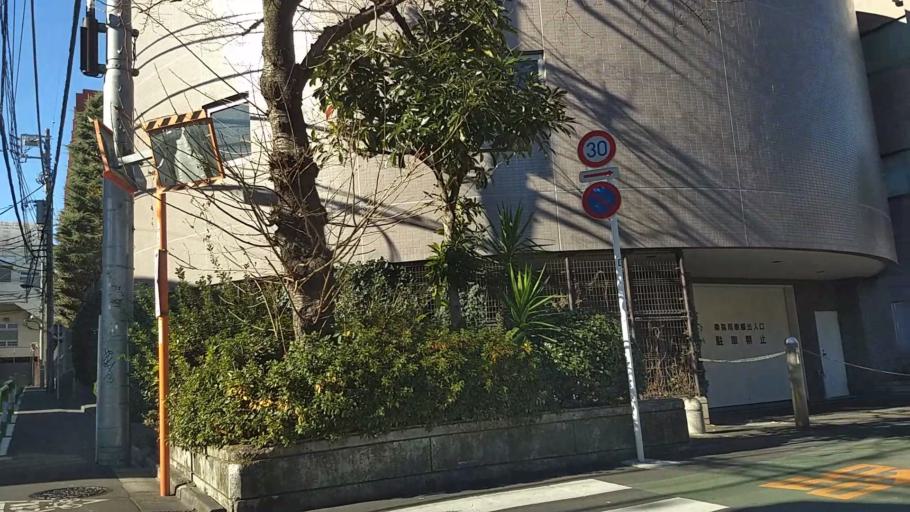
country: JP
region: Tokyo
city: Tokyo
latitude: 35.7047
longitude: 139.7034
